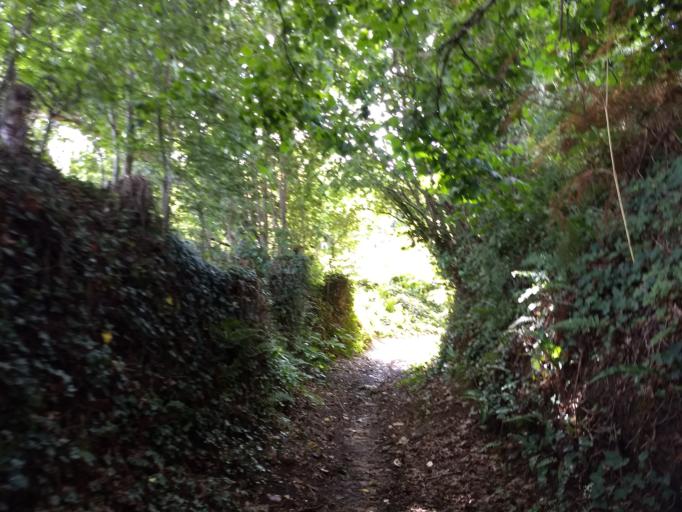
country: GB
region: England
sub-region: Isle of Wight
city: Newport
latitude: 50.6805
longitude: -1.2966
